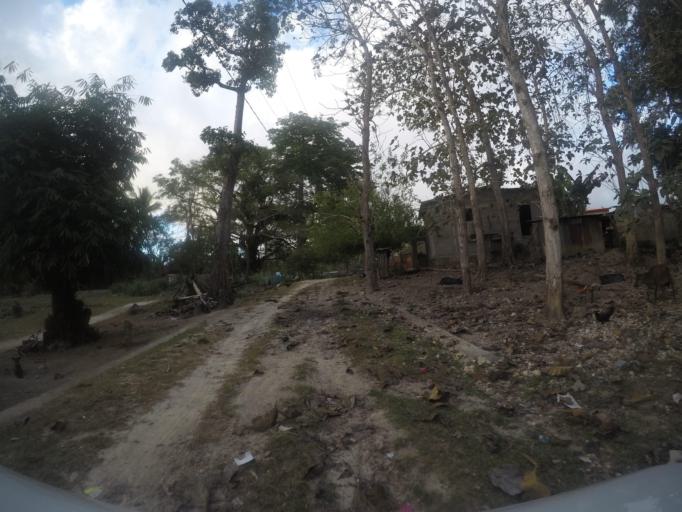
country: TL
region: Lautem
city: Lospalos
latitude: -8.5159
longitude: 126.9872
